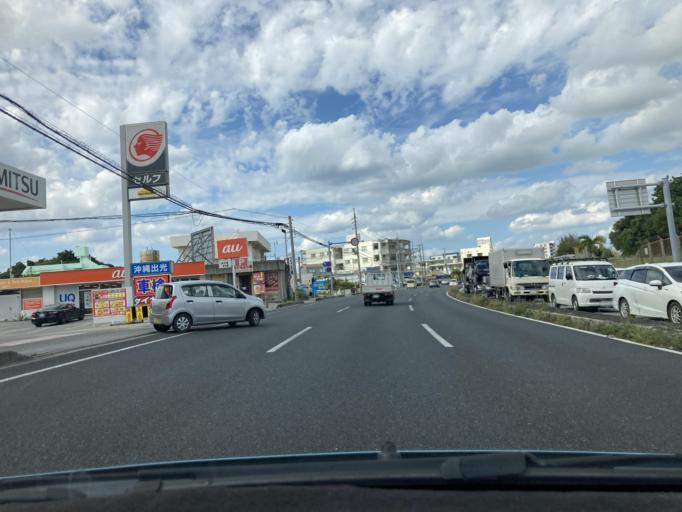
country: JP
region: Okinawa
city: Chatan
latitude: 26.3281
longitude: 127.7525
